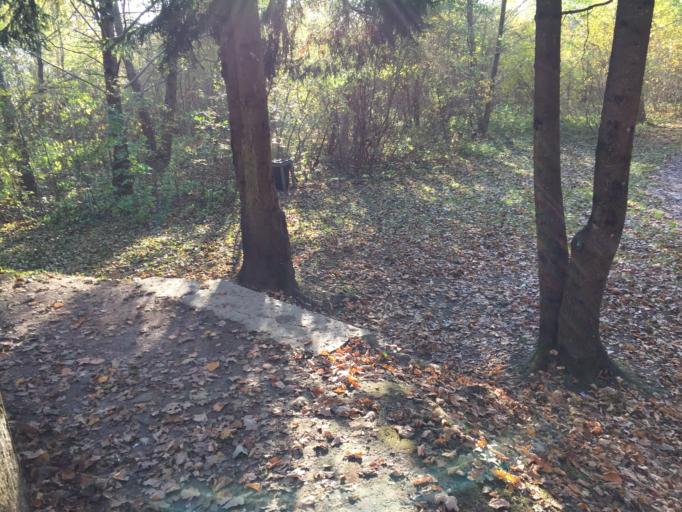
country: LT
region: Klaipedos apskritis
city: Kretinga
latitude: 55.8939
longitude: 21.2091
